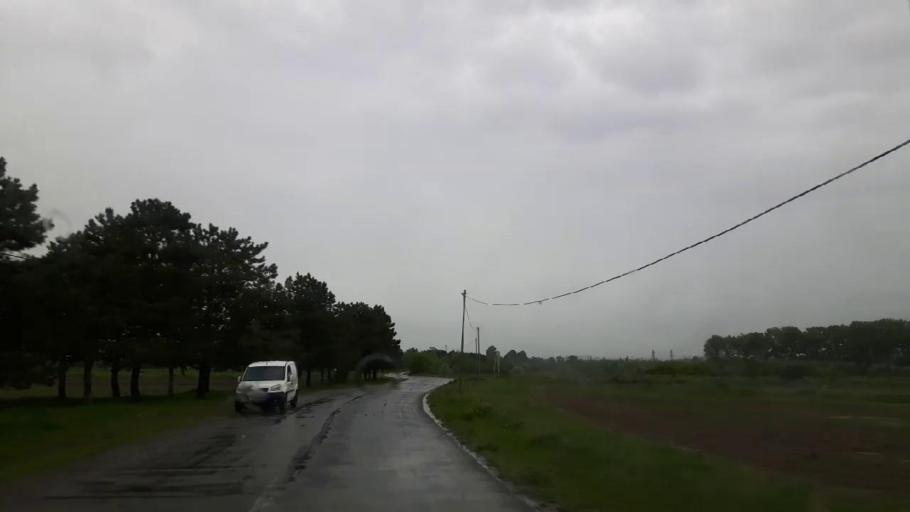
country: GE
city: Agara
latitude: 42.0201
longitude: 43.9042
